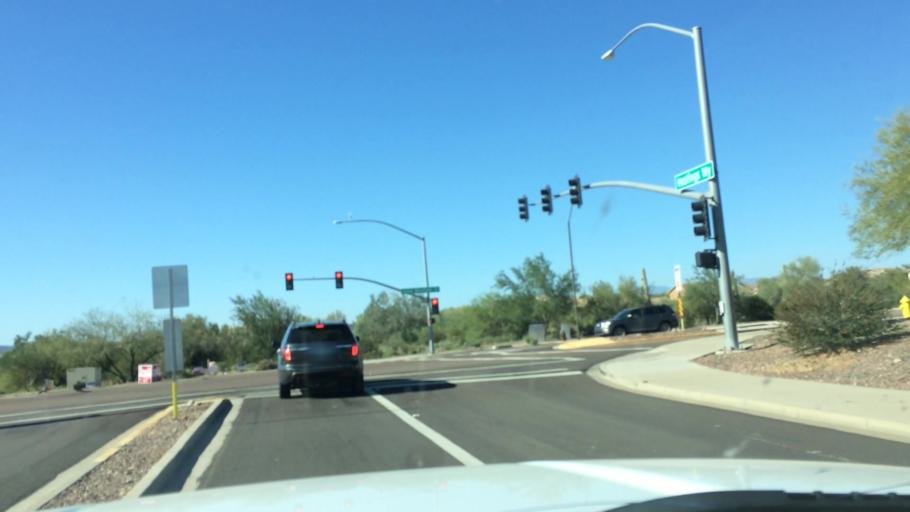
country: US
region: Arizona
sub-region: Maricopa County
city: Anthem
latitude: 33.8502
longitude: -112.1161
